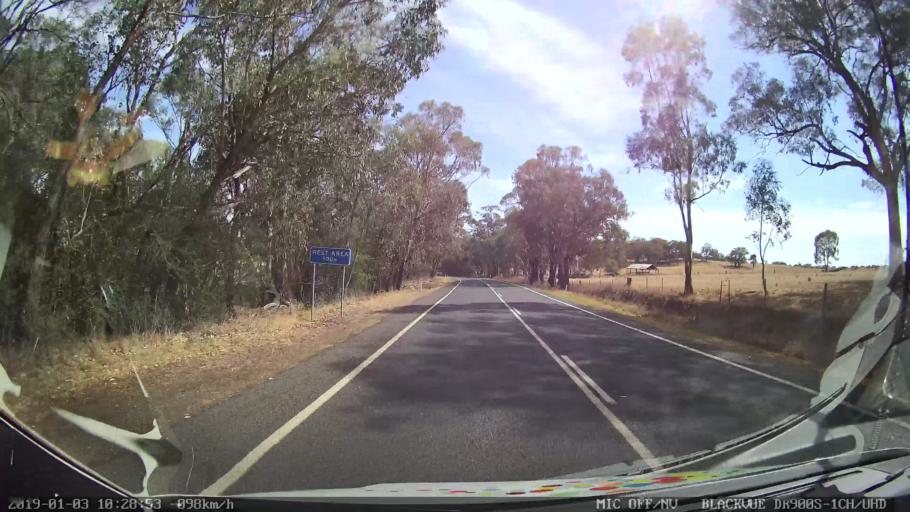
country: AU
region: New South Wales
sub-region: Young
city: Young
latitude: -34.3816
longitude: 148.2600
